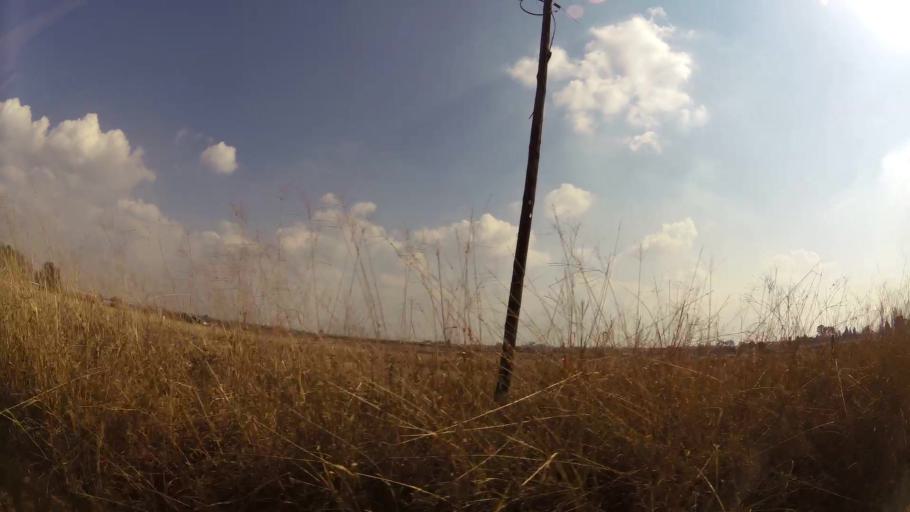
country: ZA
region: Gauteng
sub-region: Ekurhuleni Metropolitan Municipality
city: Springs
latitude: -26.2023
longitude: 28.5371
